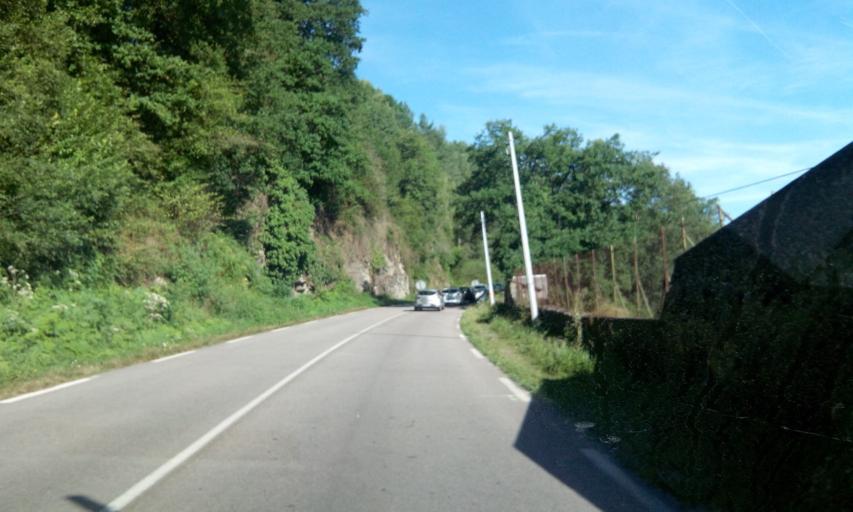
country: FR
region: Limousin
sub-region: Departement de la Haute-Vienne
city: Saint-Leonard-de-Noblat
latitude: 45.8370
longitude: 1.4690
